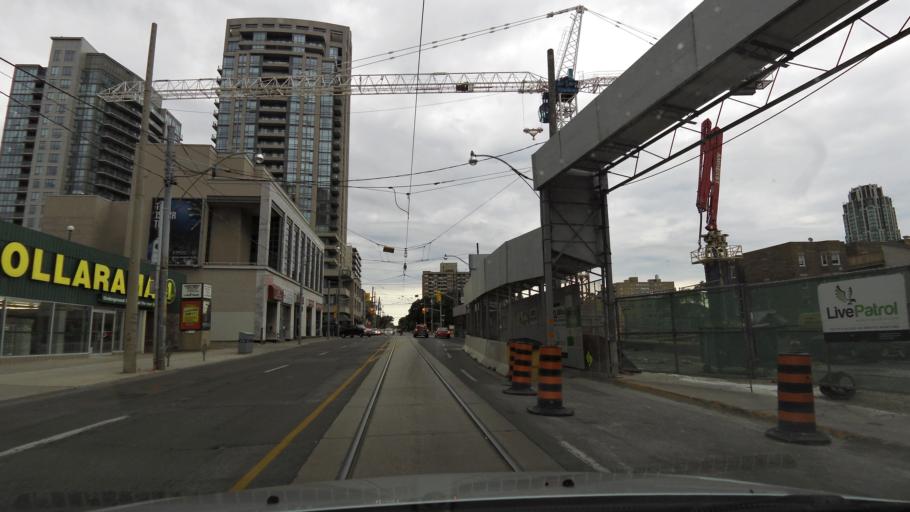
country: CA
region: Ontario
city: Toronto
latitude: 43.6823
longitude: -79.4180
